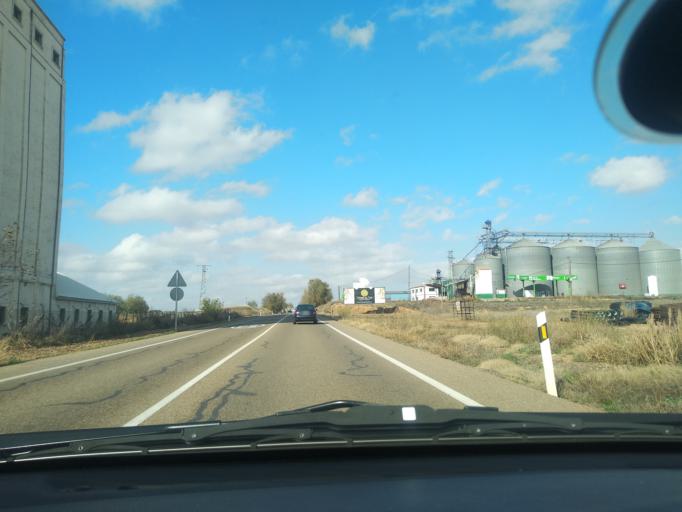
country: ES
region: Castille and Leon
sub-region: Provincia de Valladolid
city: Medina de Rioseco
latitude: 41.8927
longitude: -5.0545
